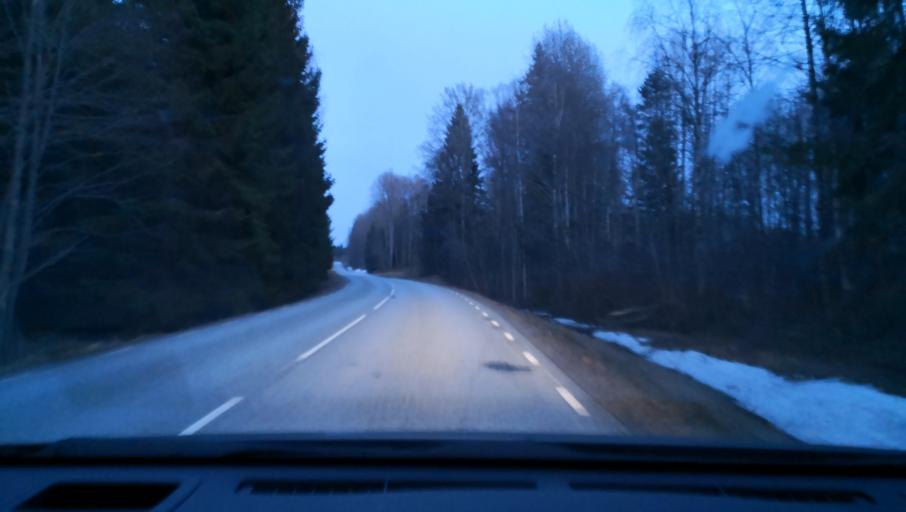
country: SE
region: OErebro
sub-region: Lindesbergs Kommun
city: Frovi
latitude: 59.5934
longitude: 15.4229
